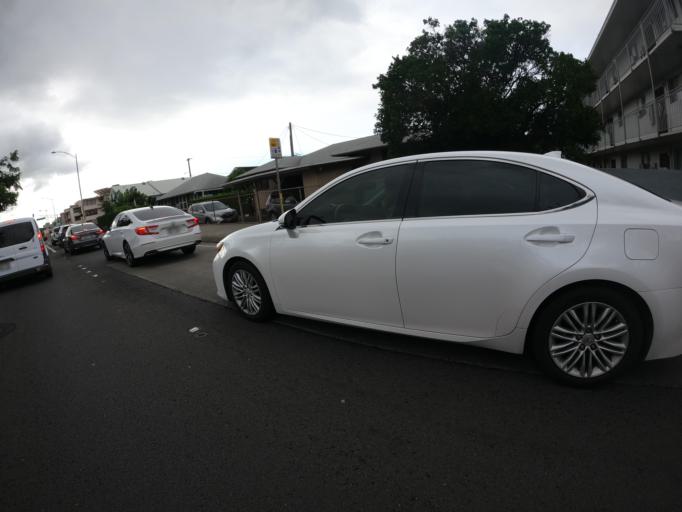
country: US
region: Hawaii
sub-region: Honolulu County
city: Honolulu
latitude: 21.3223
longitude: -157.8640
